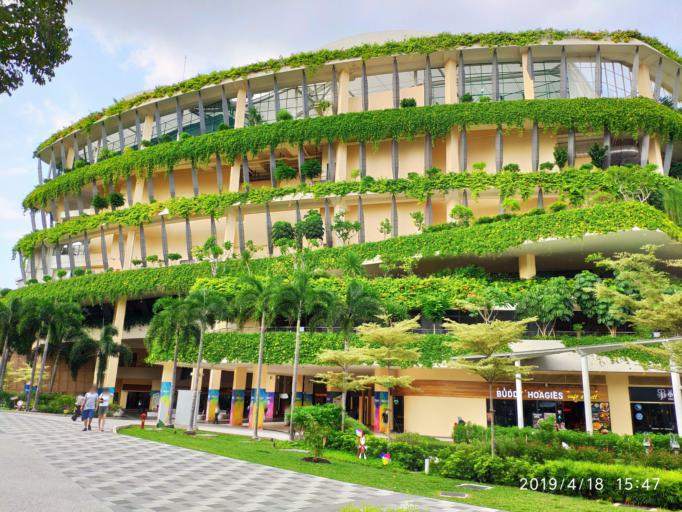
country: SG
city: Singapore
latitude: 1.3263
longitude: 103.9312
